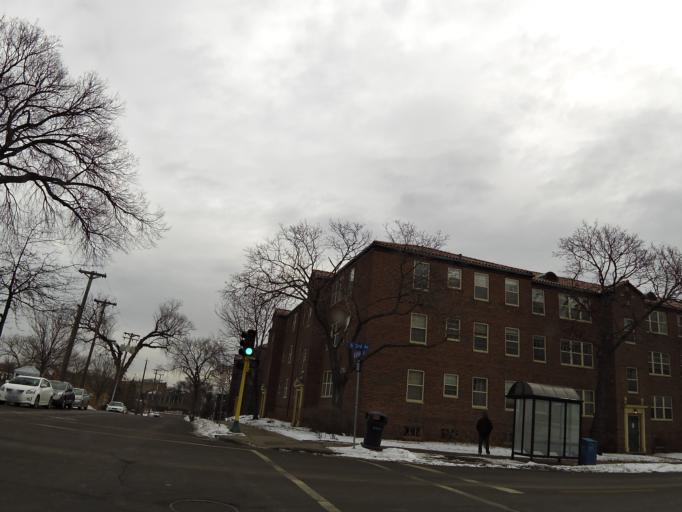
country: US
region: Minnesota
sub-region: Hennepin County
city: Minneapolis
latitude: 44.9592
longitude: -93.2729
